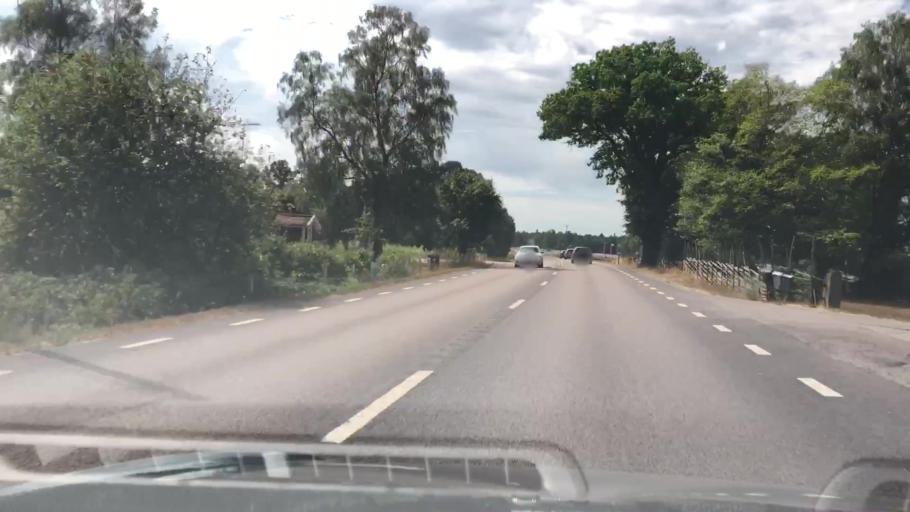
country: SE
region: Kalmar
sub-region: Torsas Kommun
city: Torsas
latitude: 56.3696
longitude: 16.0657
